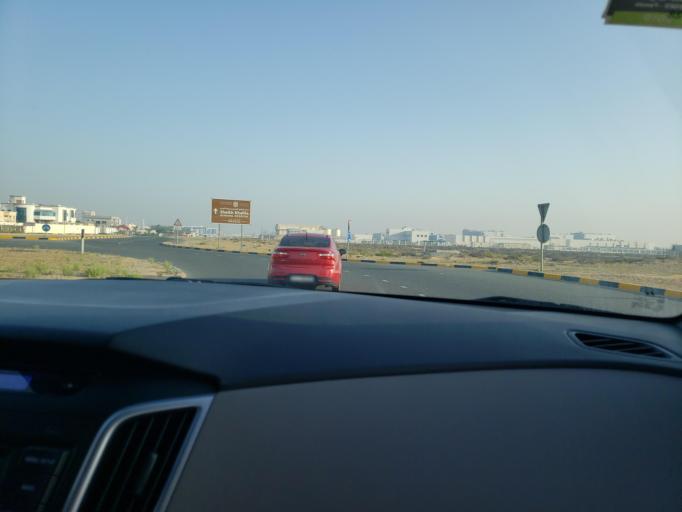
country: AE
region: Umm al Qaywayn
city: Umm al Qaywayn
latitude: 25.4963
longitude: 55.5985
